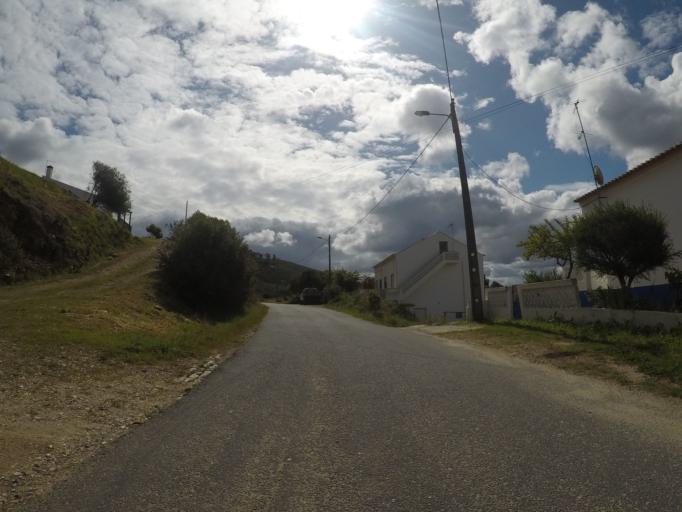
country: PT
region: Beja
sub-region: Odemira
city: Sao Teotonio
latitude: 37.4363
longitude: -8.7672
